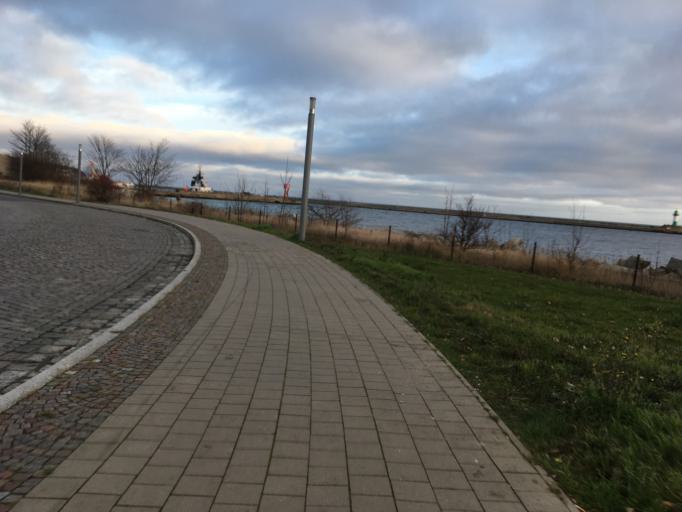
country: DE
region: Mecklenburg-Vorpommern
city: Sassnitz
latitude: 54.5075
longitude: 13.6310
